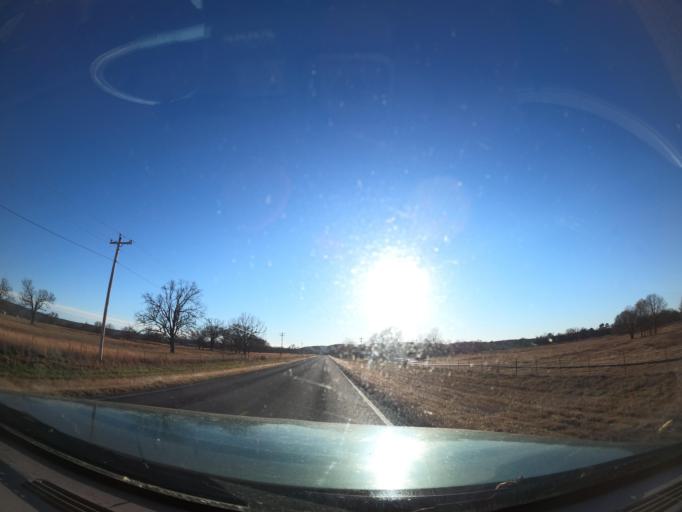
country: US
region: Oklahoma
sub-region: Latimer County
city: Wilburton
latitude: 34.9027
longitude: -95.4304
